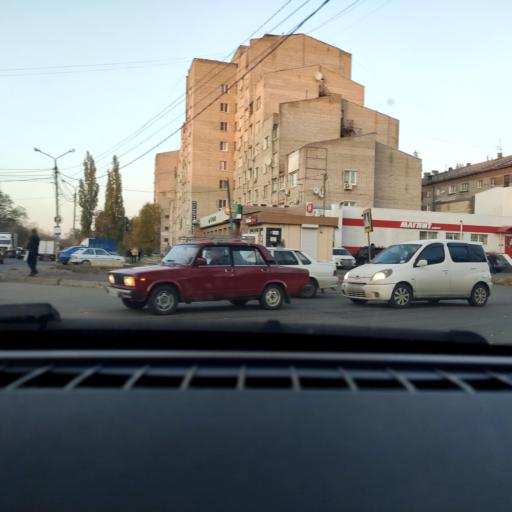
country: RU
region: Voronezj
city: Maslovka
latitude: 51.5988
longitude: 39.2525
